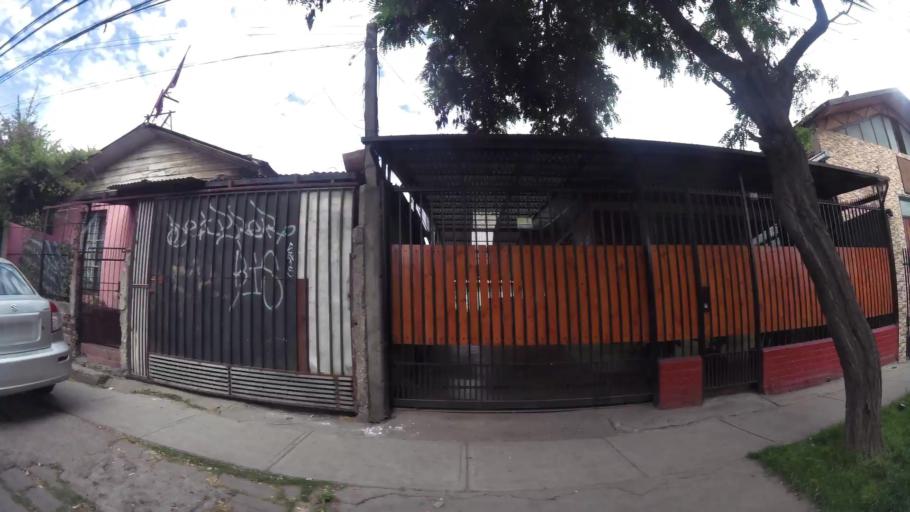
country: CL
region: Santiago Metropolitan
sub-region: Provincia de Santiago
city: La Pintana
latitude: -33.5797
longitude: -70.6386
